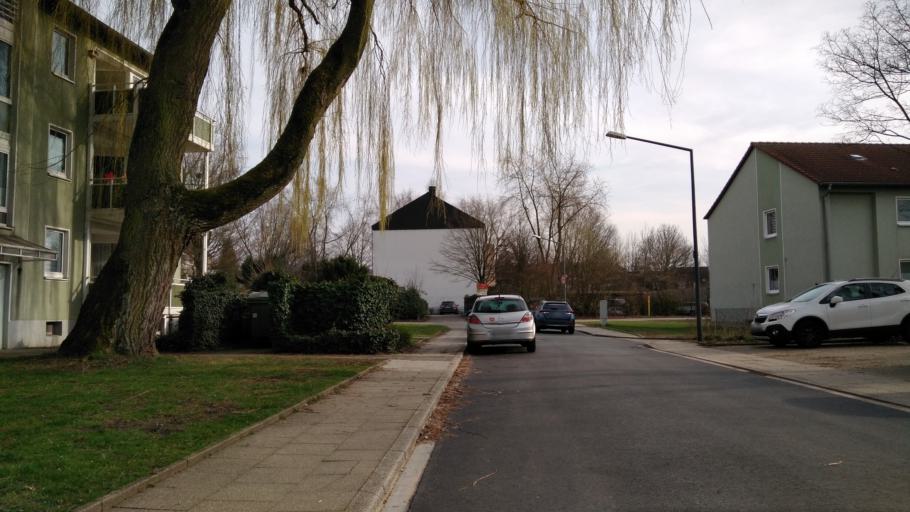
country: DE
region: North Rhine-Westphalia
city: Herten
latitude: 51.6102
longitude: 7.1265
